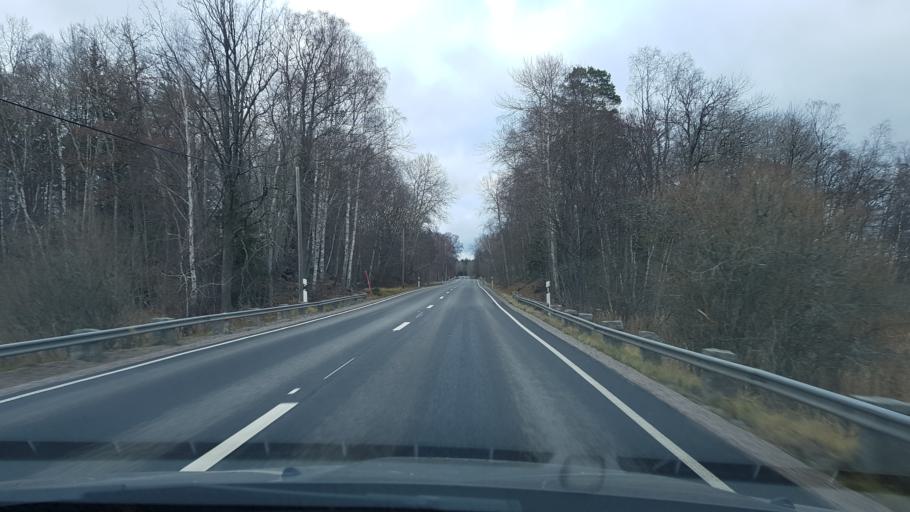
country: SE
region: Stockholm
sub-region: Norrtalje Kommun
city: Skanninge
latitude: 60.0123
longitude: 18.3388
